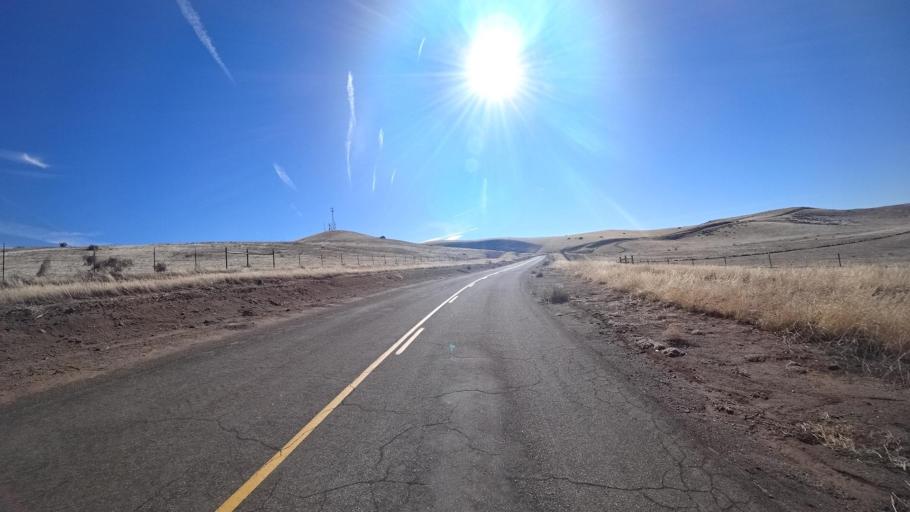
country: US
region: California
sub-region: Kern County
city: Maricopa
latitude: 34.9250
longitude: -119.4101
